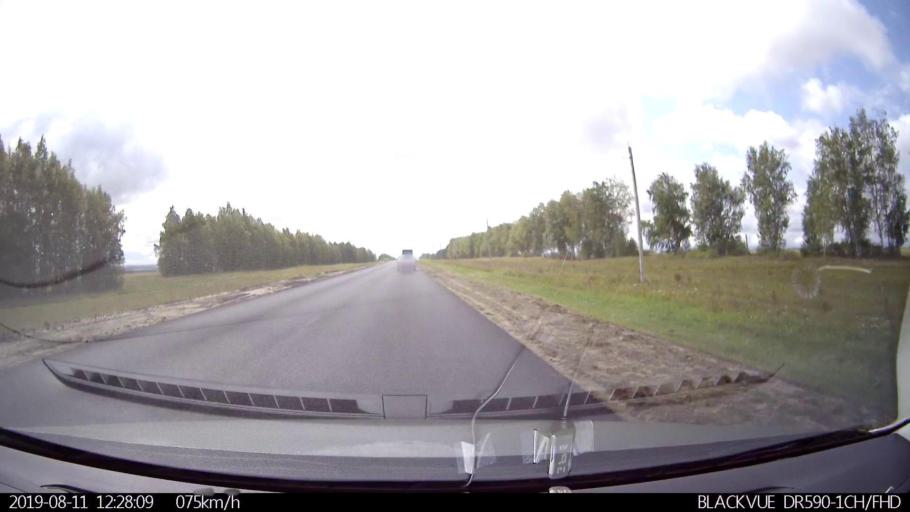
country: RU
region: Ulyanovsk
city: Ignatovka
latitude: 53.8466
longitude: 47.9140
